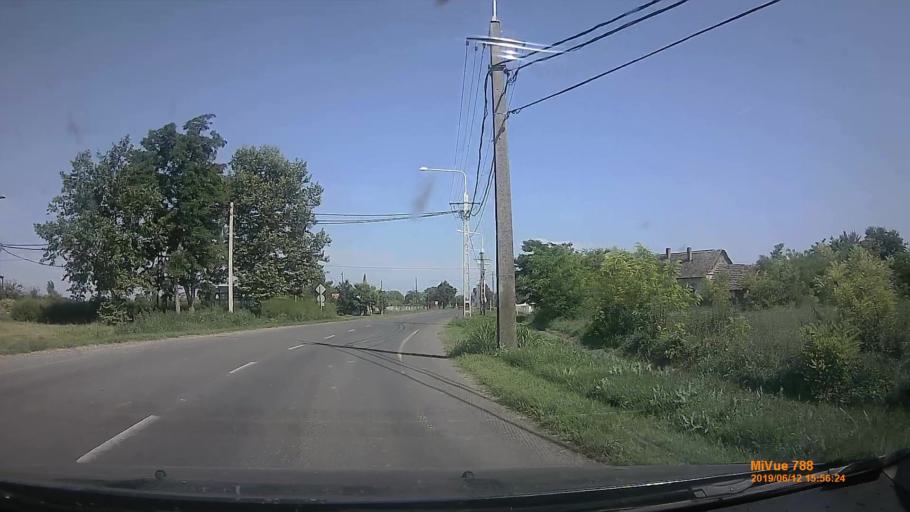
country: HU
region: Csongrad
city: Apatfalva
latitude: 46.1699
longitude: 20.6191
